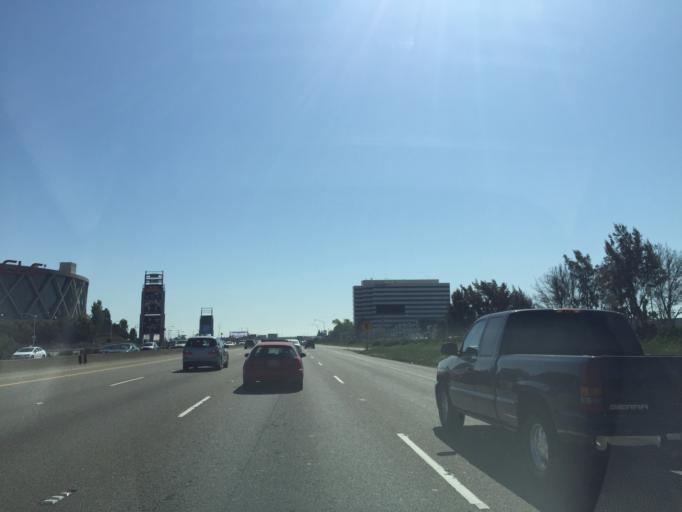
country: US
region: California
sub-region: Alameda County
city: Alameda
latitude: 37.7514
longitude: -122.2061
